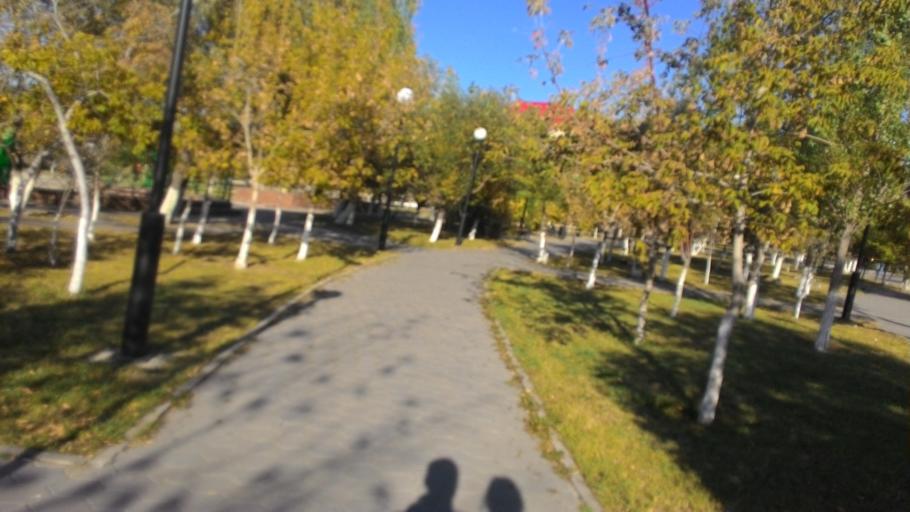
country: KZ
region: Astana Qalasy
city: Astana
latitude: 51.1821
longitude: 71.4123
